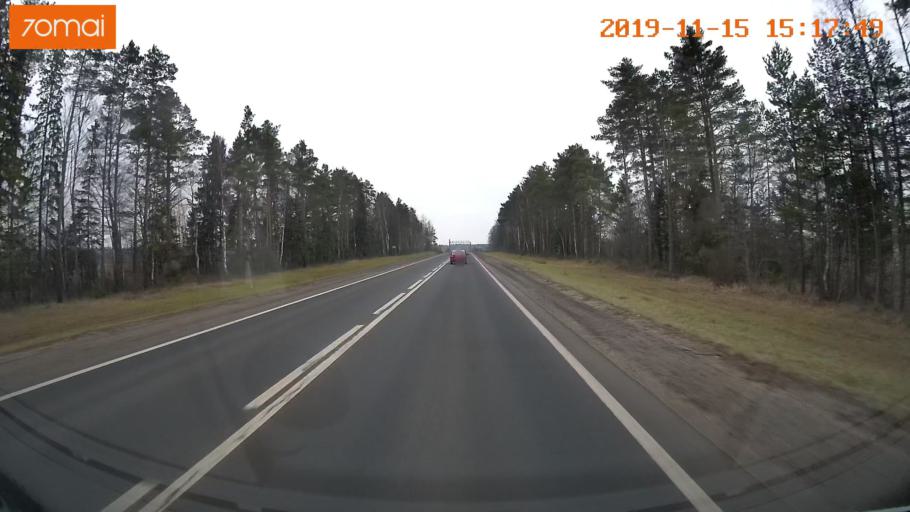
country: RU
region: Jaroslavl
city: Danilov
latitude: 58.2552
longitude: 40.1808
